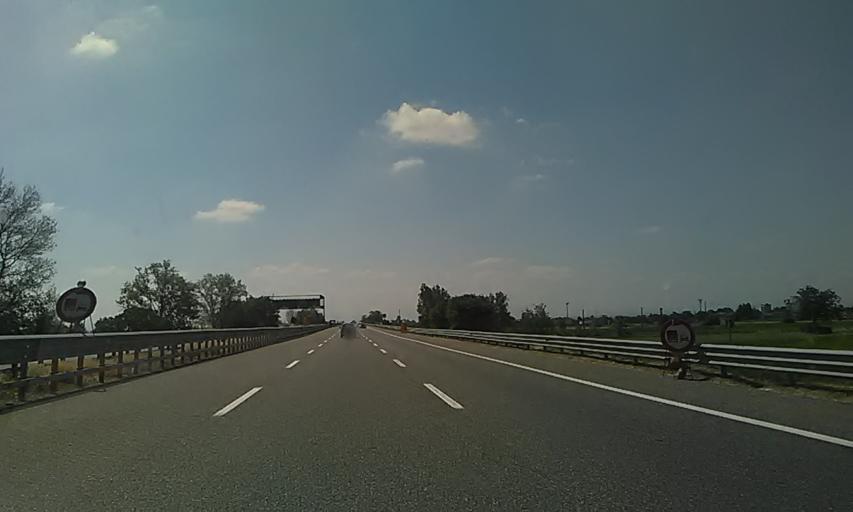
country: IT
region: Piedmont
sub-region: Provincia di Alessandria
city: Castellazzo Bormida
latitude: 44.8565
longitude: 8.5865
